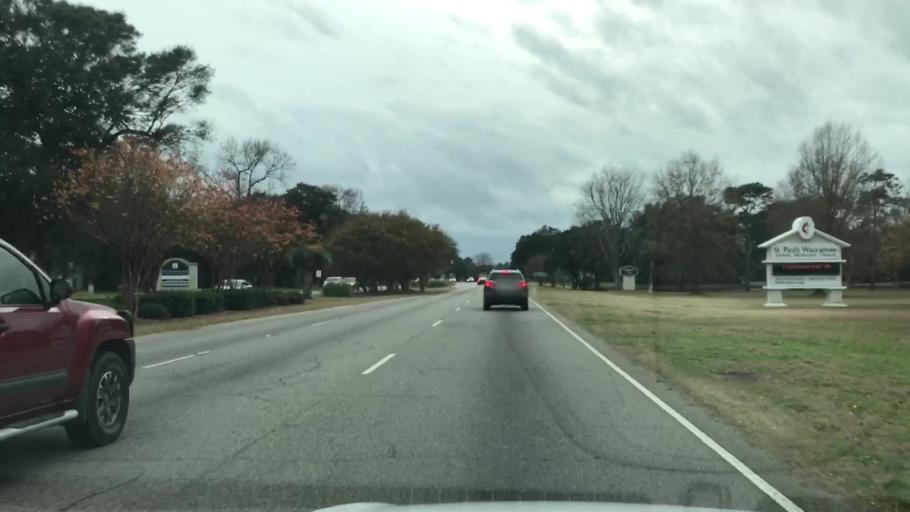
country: US
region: South Carolina
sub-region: Georgetown County
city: Murrells Inlet
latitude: 33.4859
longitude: -79.0947
